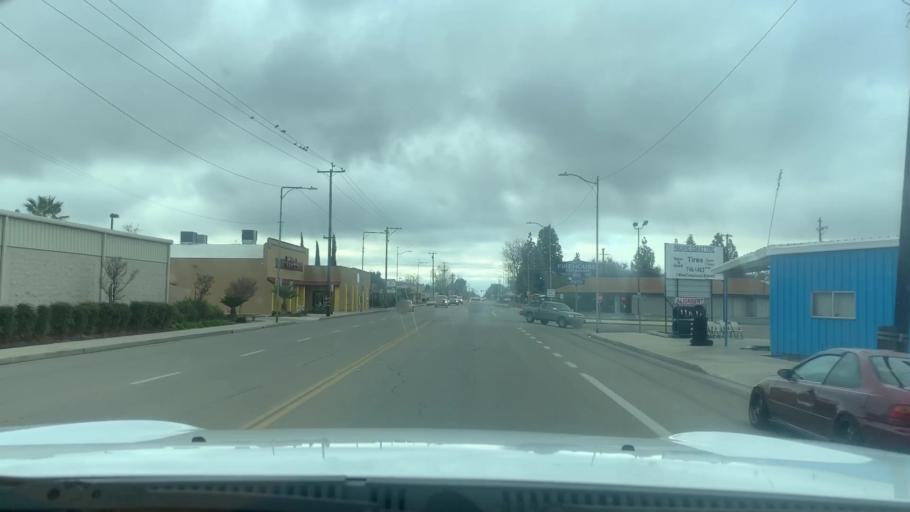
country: US
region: California
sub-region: Kern County
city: Shafter
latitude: 35.4998
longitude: -119.2718
